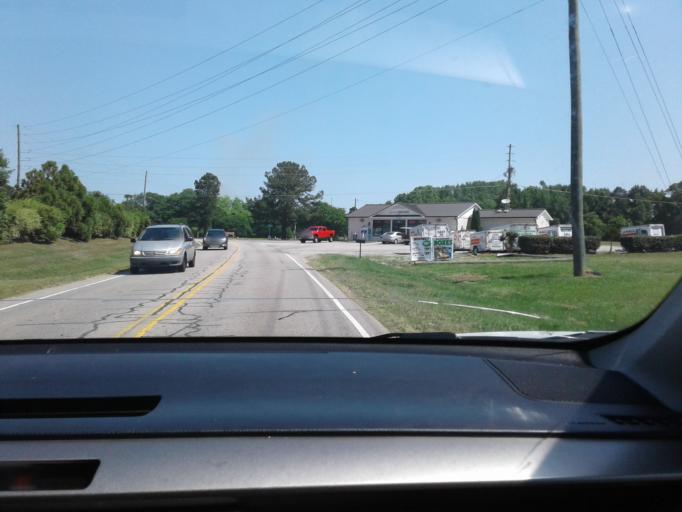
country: US
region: North Carolina
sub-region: Wake County
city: Fuquay-Varina
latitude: 35.5967
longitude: -78.8371
